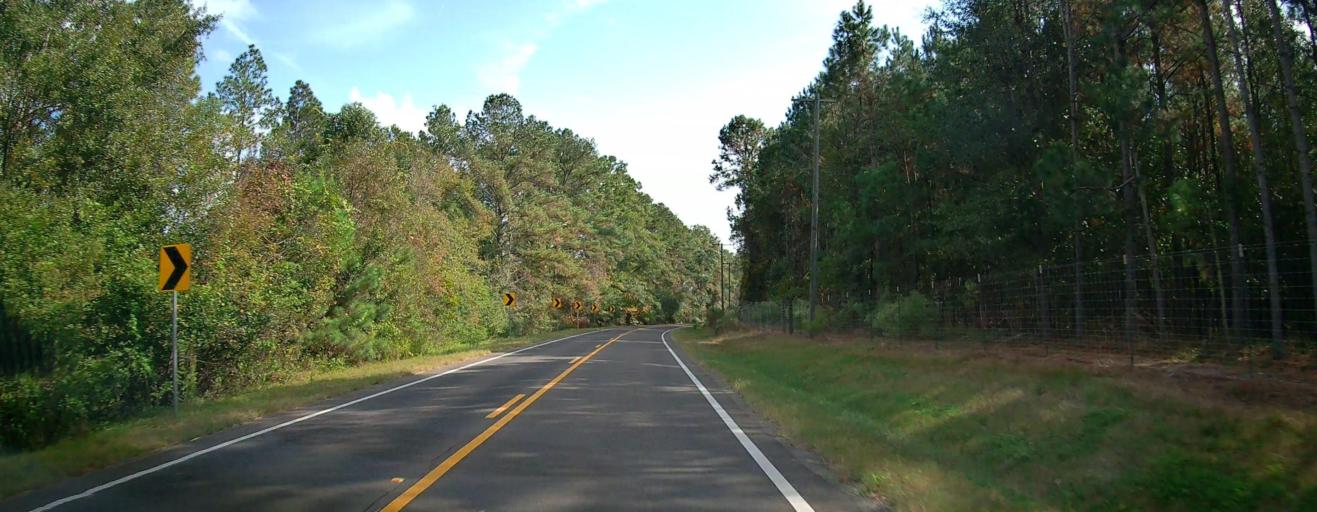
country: US
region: Georgia
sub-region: Thomas County
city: Thomasville
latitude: 30.9231
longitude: -84.0146
